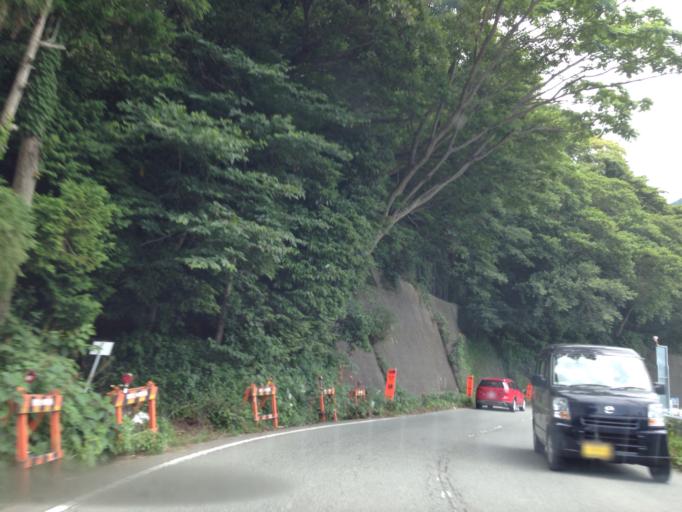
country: JP
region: Shizuoka
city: Heda
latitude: 34.9083
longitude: 138.8185
